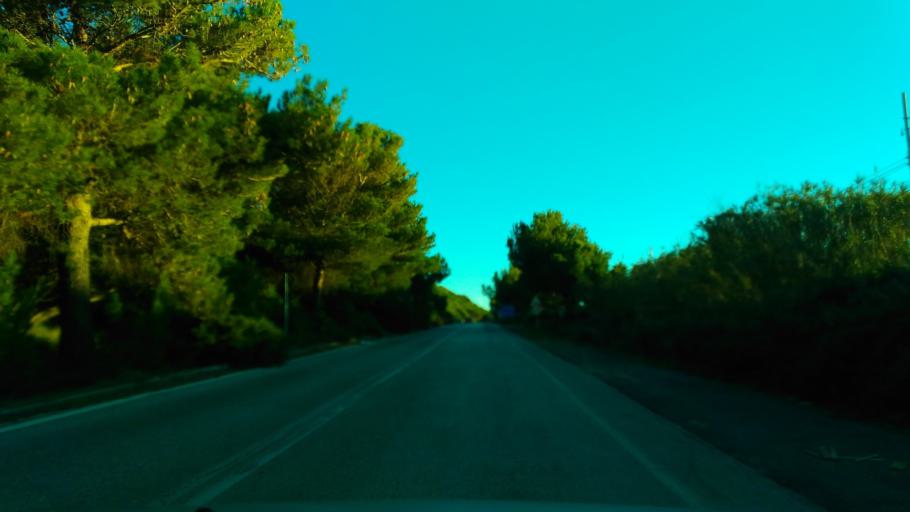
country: IT
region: Tuscany
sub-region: Provincia di Livorno
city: Quercianella
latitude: 43.4483
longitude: 10.3807
